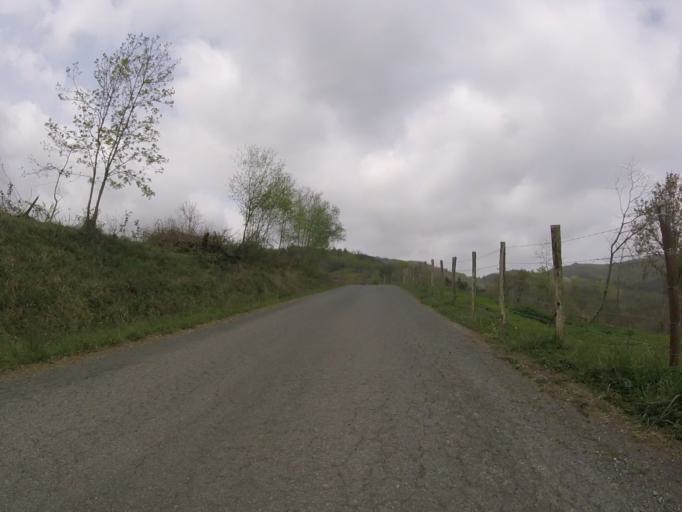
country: ES
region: Basque Country
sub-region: Provincia de Guipuzcoa
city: Zizurkil
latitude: 43.2161
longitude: -2.0866
